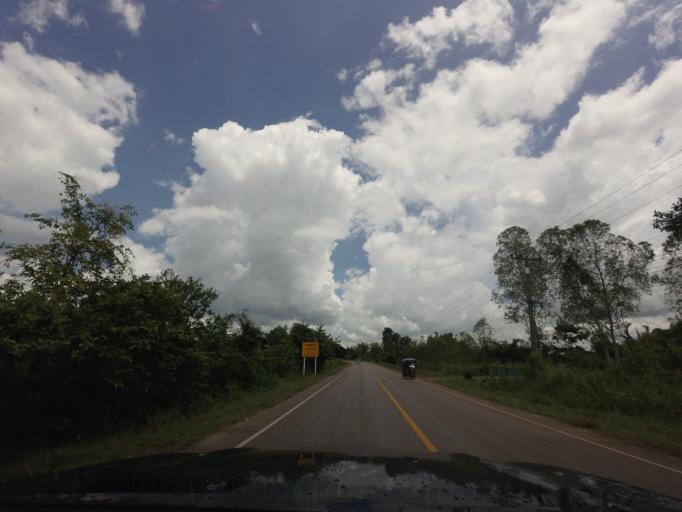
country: TH
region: Changwat Udon Thani
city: Phen
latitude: 17.5472
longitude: 102.8778
